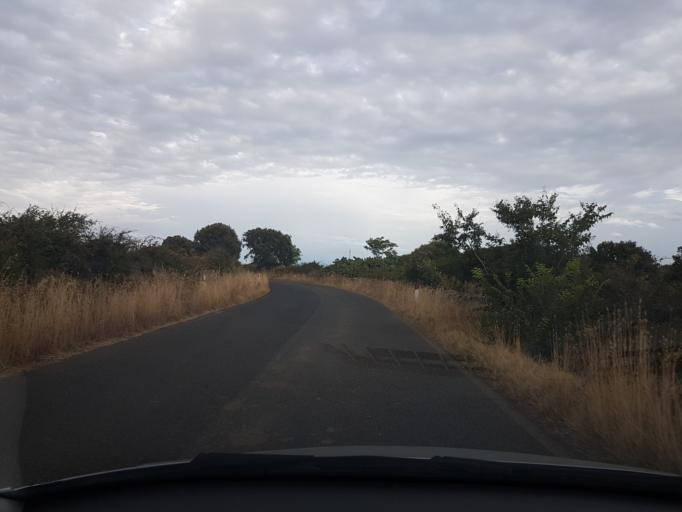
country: IT
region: Sardinia
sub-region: Provincia di Oristano
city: Seneghe
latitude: 40.0769
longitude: 8.6054
